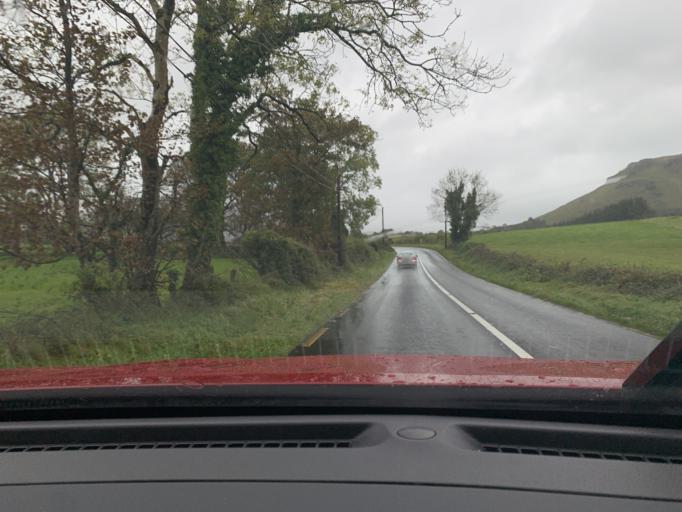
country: IE
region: Connaught
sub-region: Sligo
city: Sligo
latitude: 54.3078
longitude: -8.4338
